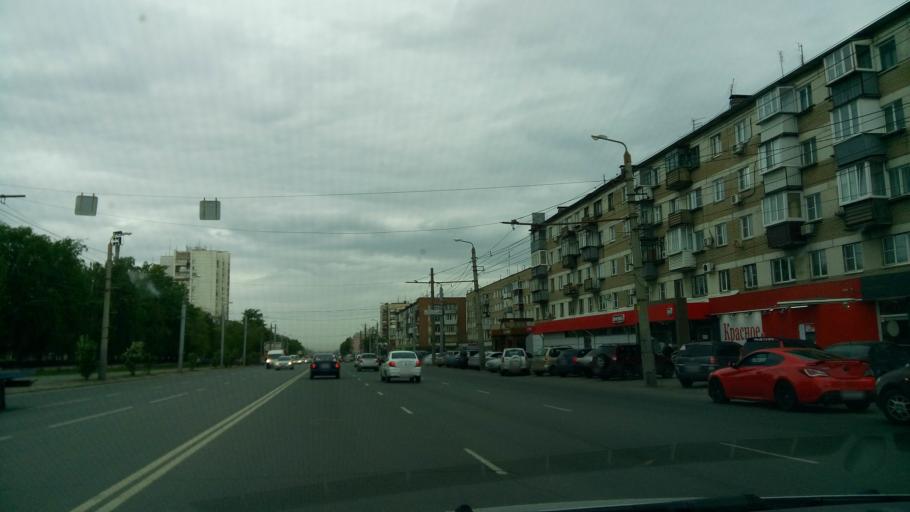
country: RU
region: Chelyabinsk
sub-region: Gorod Chelyabinsk
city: Chelyabinsk
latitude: 55.1799
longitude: 61.3873
